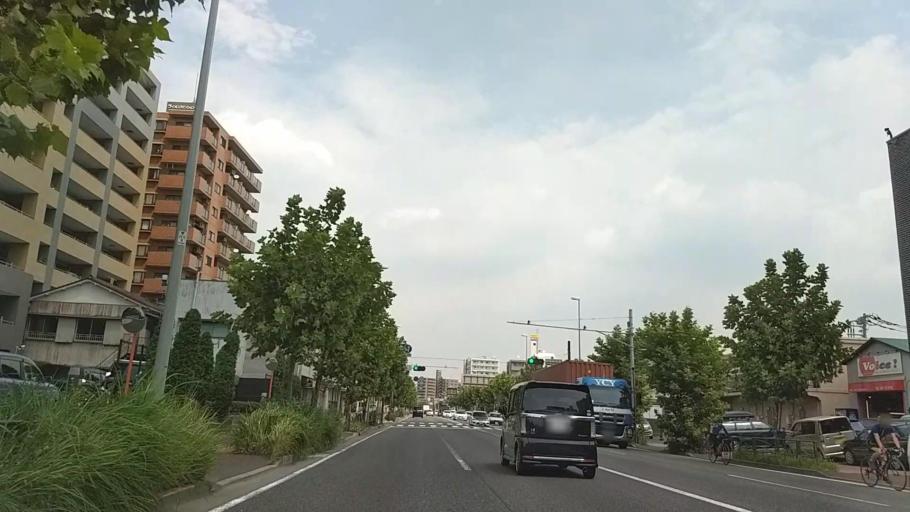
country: JP
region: Kanagawa
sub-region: Kawasaki-shi
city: Kawasaki
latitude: 35.4966
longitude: 139.6705
